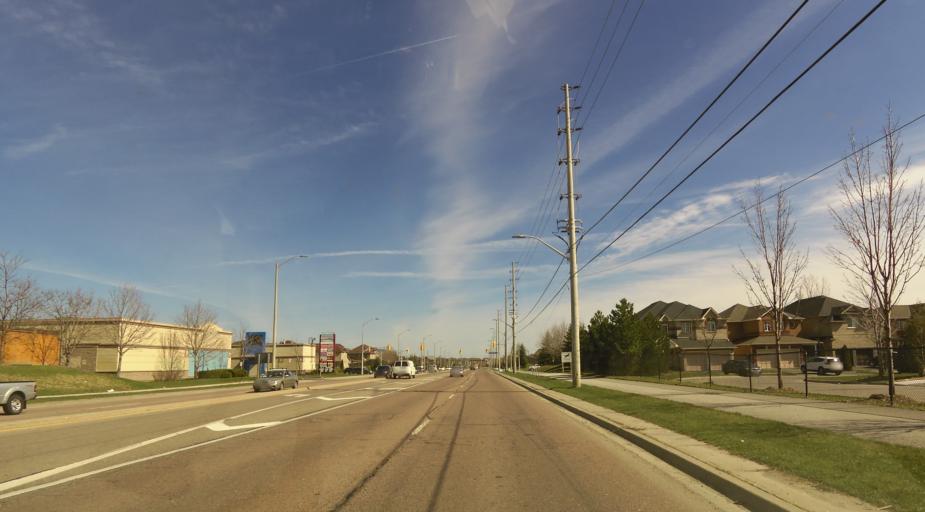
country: CA
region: Ontario
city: Brampton
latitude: 43.6381
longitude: -79.7296
